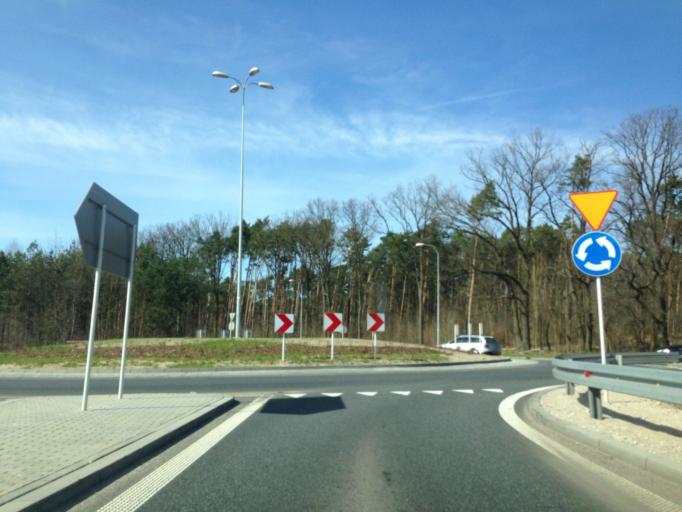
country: PL
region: Lodz Voivodeship
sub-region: Powiat sieradzki
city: Sieradz
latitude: 51.6025
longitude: 18.8122
